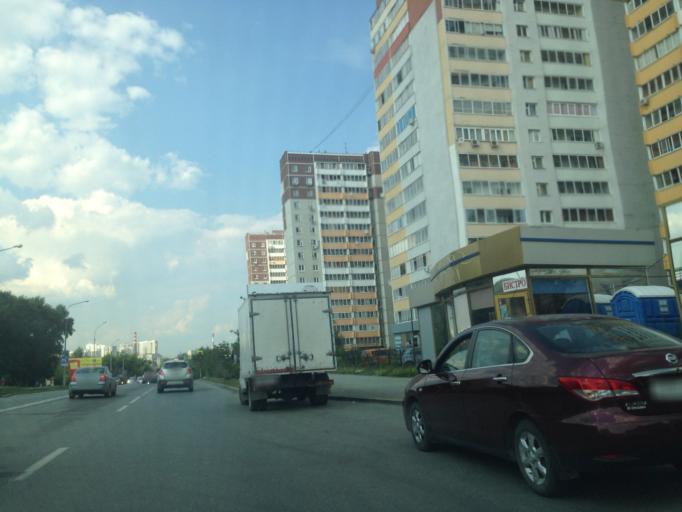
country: RU
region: Sverdlovsk
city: Yekaterinburg
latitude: 56.8632
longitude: 60.6330
